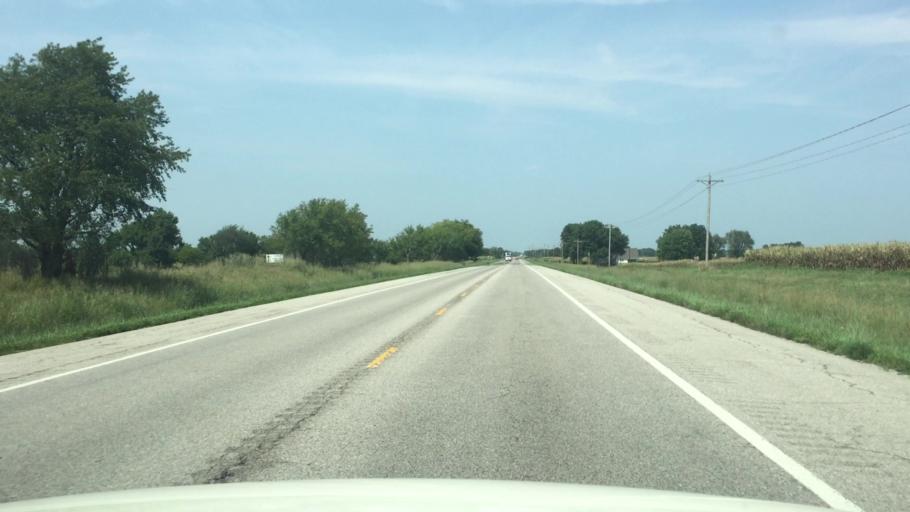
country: US
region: Kansas
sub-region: Crawford County
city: Pittsburg
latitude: 37.2735
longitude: -94.7053
